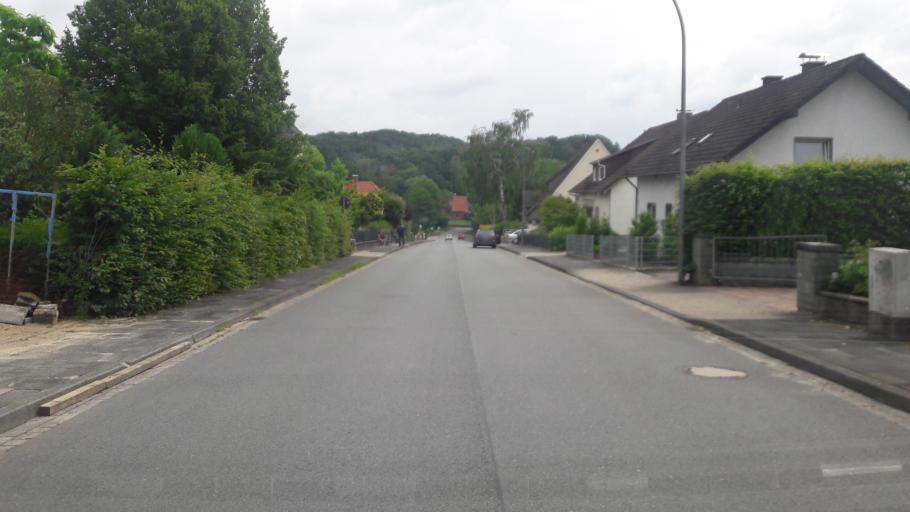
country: DE
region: North Rhine-Westphalia
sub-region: Regierungsbezirk Detmold
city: Lage
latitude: 51.9430
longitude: 8.7739
